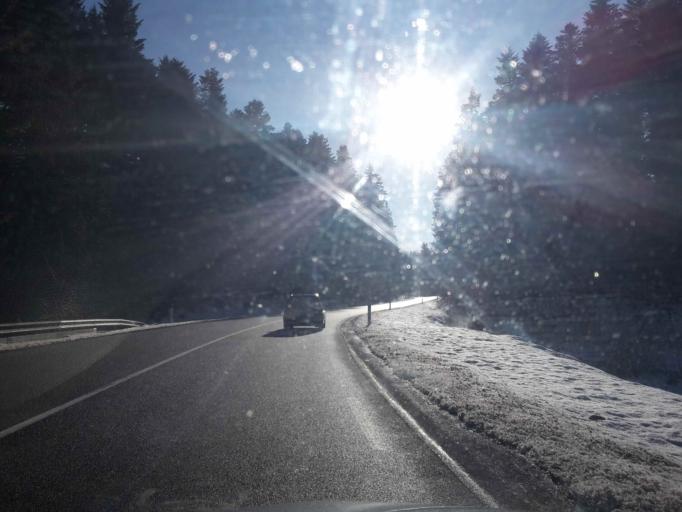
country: FR
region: Franche-Comte
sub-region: Departement du Doubs
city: Doubs
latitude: 47.0304
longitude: 6.3341
